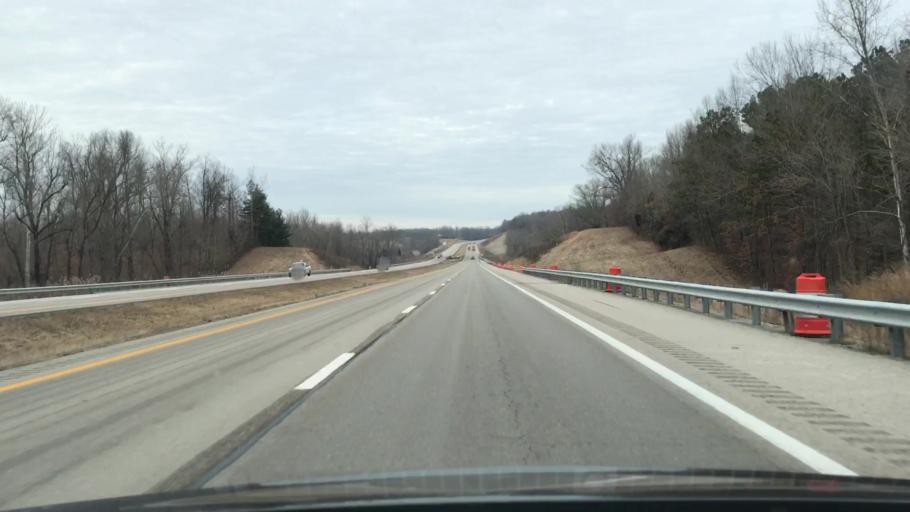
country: US
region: Kentucky
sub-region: Ohio County
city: Hartford
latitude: 37.4726
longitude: -86.8966
